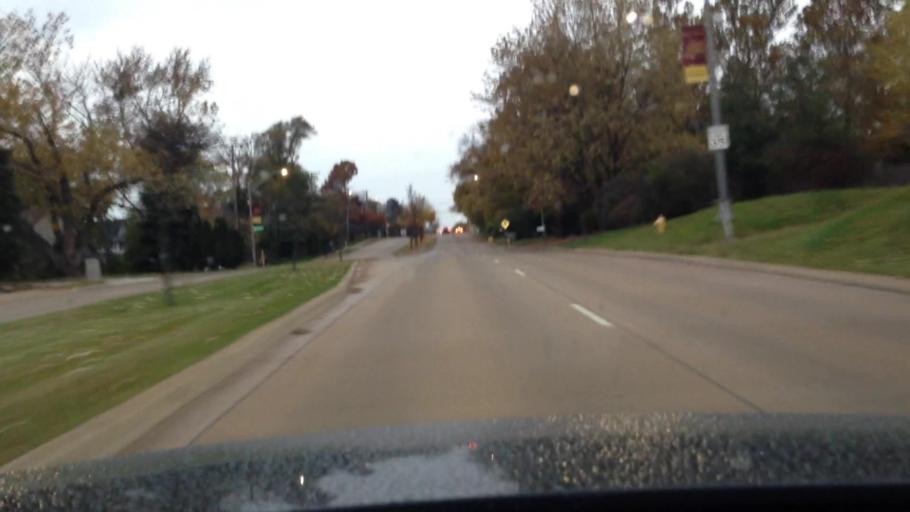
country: US
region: Illinois
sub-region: DuPage County
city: Lombard
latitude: 41.8483
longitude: -88.0166
